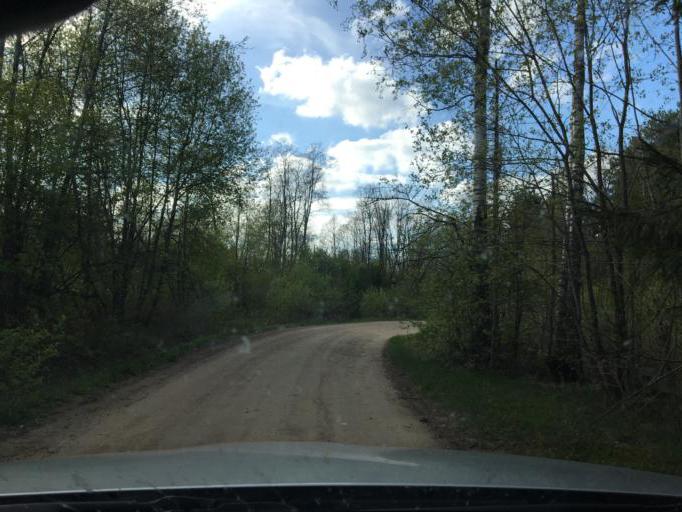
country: LV
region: Ozolnieku
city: Ozolnieki
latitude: 56.6710
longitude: 23.8738
